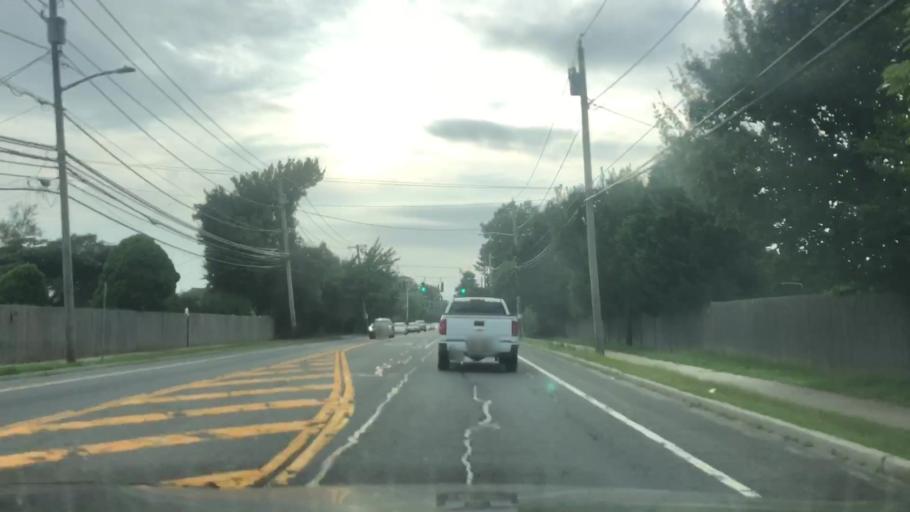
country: US
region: New York
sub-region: Nassau County
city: North Wantagh
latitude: 40.6929
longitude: -73.5125
